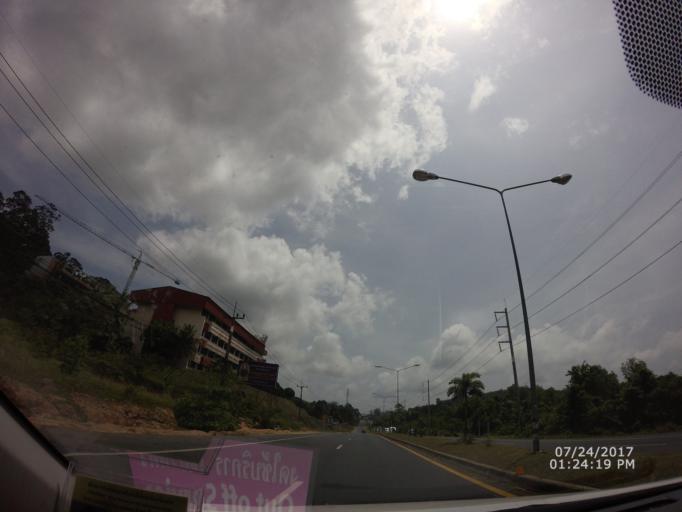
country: TH
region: Phuket
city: Thalang
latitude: 8.0901
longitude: 98.3256
